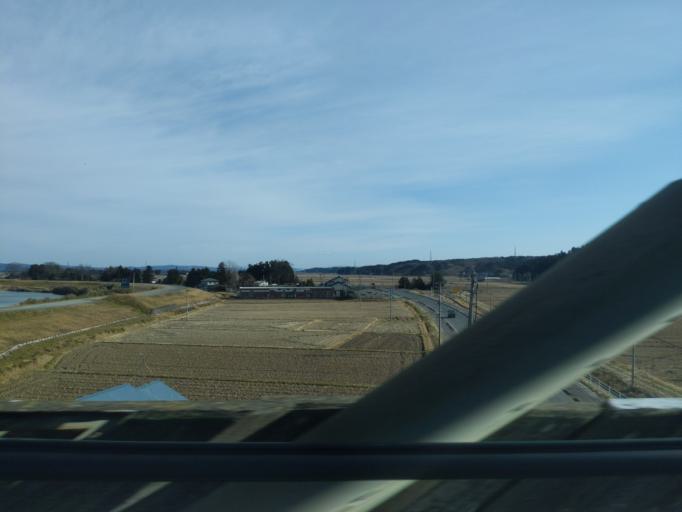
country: JP
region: Miyagi
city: Furukawa
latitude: 38.5233
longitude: 140.9603
